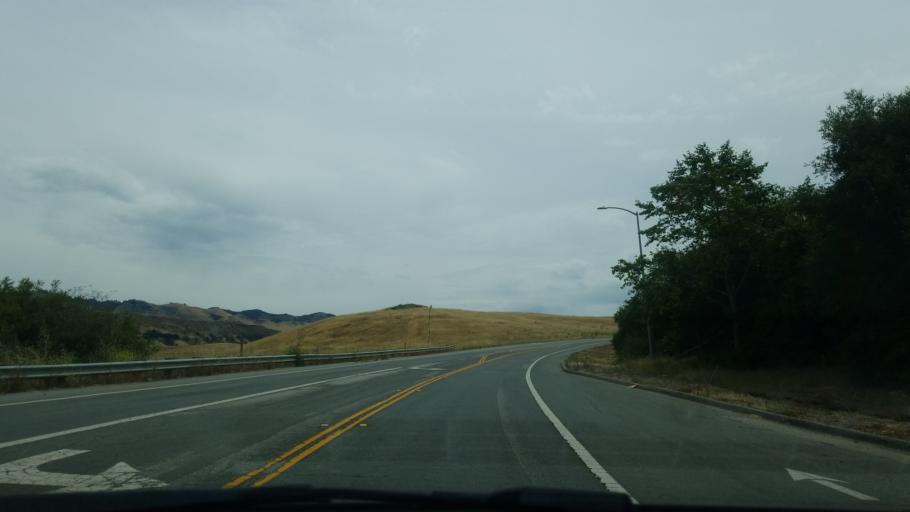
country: US
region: California
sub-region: San Luis Obispo County
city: San Luis Obispo
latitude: 35.2506
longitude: -120.6228
